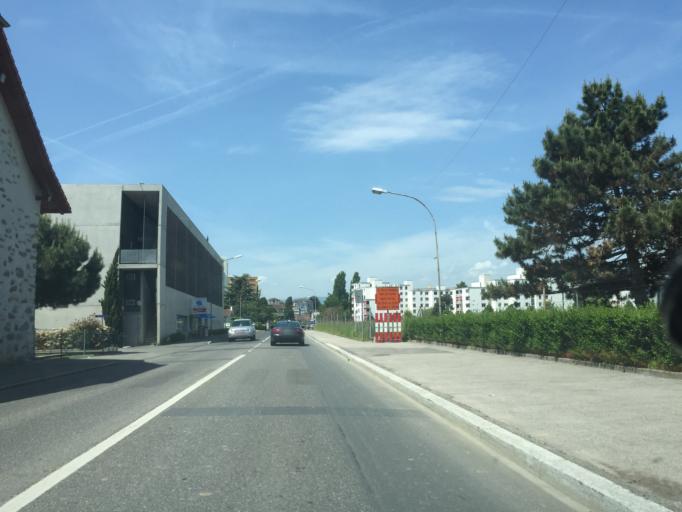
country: CH
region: Vaud
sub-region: Ouest Lausannois District
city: Chavannes
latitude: 46.5279
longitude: 6.5720
